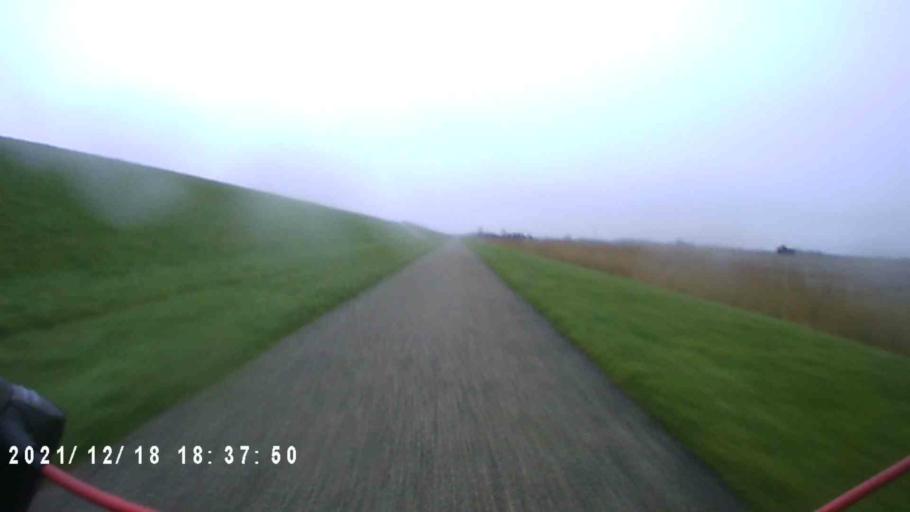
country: NL
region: Friesland
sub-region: Gemeente Dongeradeel
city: Ternaard
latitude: 53.4039
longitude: 6.0461
